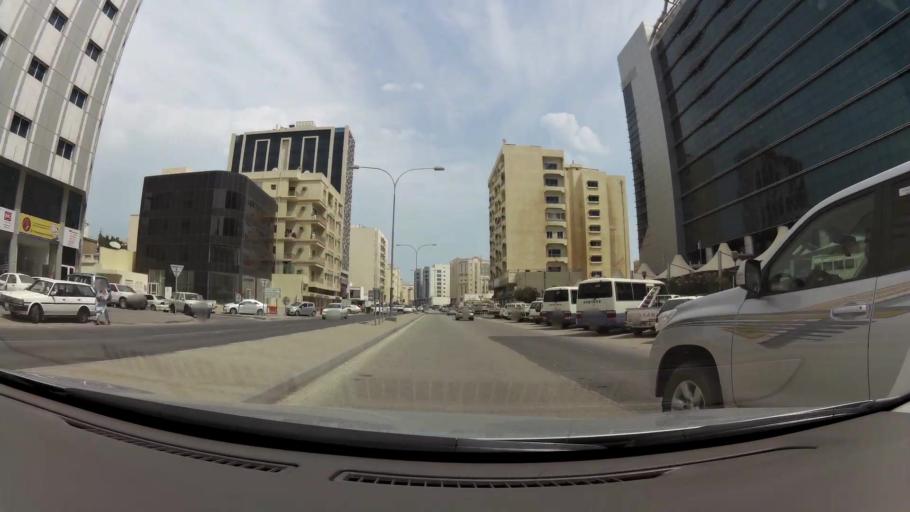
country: QA
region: Baladiyat ad Dawhah
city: Doha
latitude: 25.2749
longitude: 51.5342
